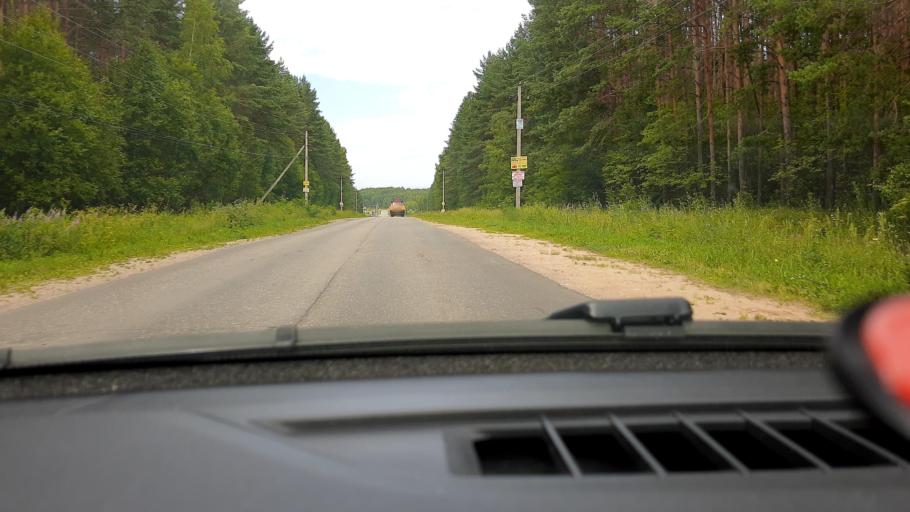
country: RU
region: Nizjnij Novgorod
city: Bogorodsk
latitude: 56.1332
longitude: 43.5921
